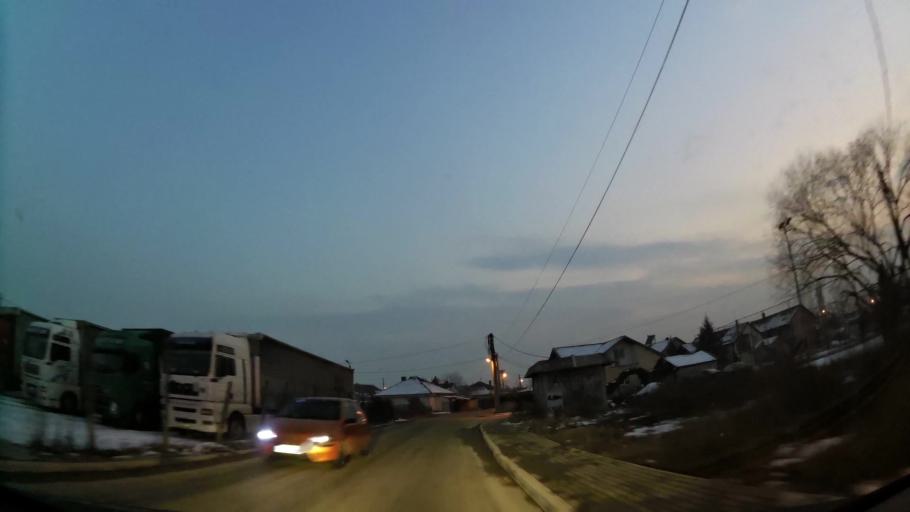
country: MK
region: Aracinovo
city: Arachinovo
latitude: 42.0023
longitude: 21.5193
